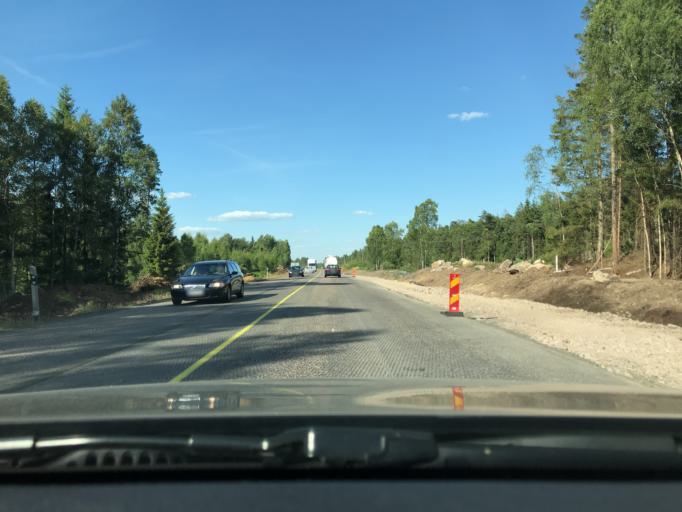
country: SE
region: Kronoberg
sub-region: Almhults Kommun
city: AElmhult
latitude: 56.5542
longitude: 14.1728
